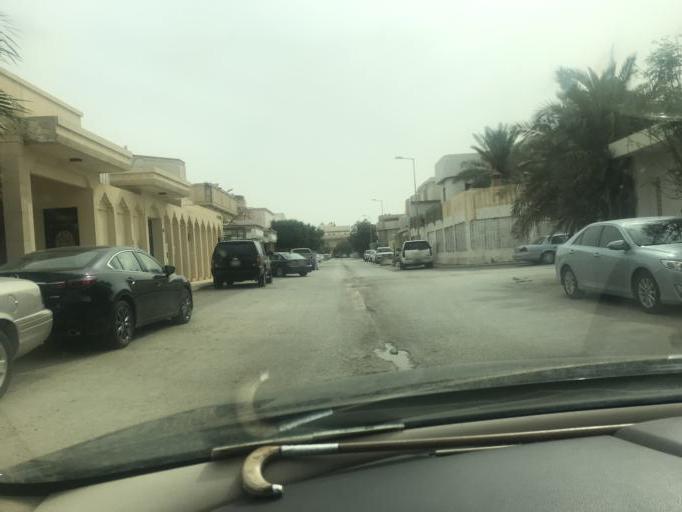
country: SA
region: Ar Riyad
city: Riyadh
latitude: 24.7497
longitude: 46.7631
